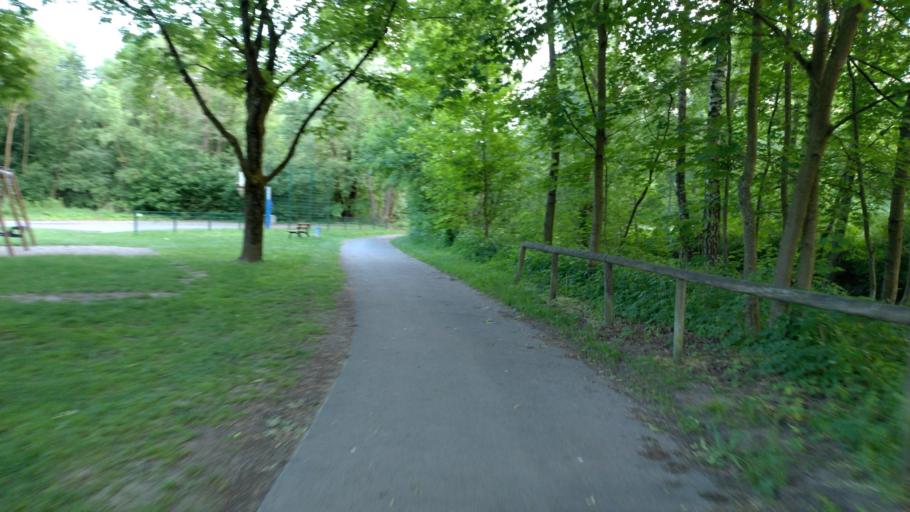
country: DE
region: Bavaria
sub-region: Upper Franconia
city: Bindlach
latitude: 49.9572
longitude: 11.6213
